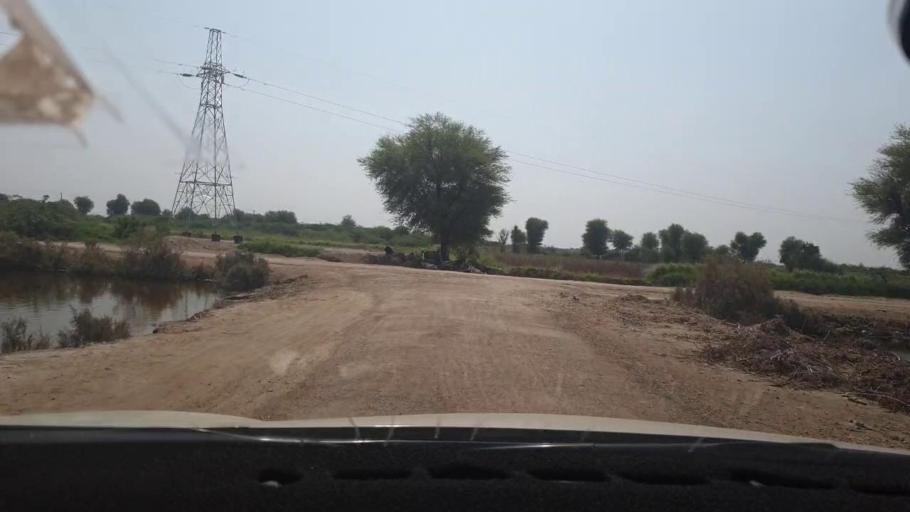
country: PK
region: Sindh
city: Tando Mittha Khan
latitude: 25.9171
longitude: 69.2348
